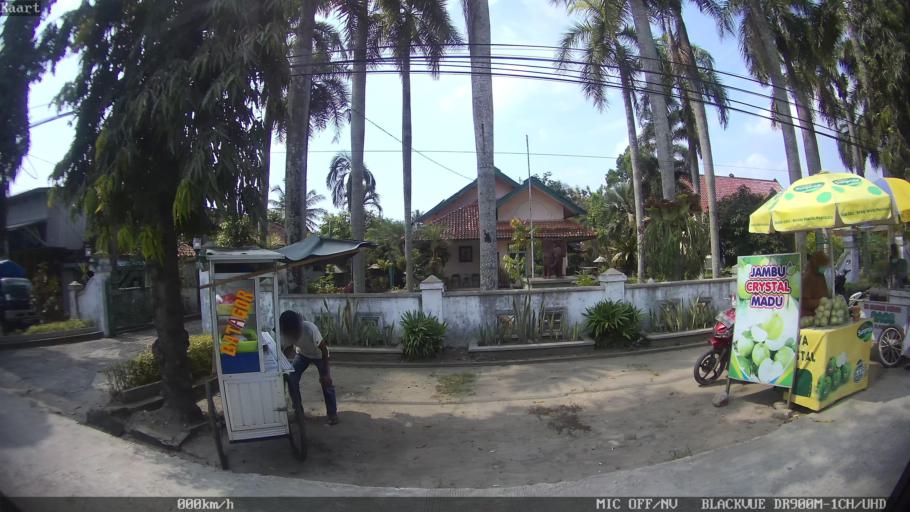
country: ID
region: Lampung
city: Pringsewu
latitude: -5.3549
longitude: 104.9691
